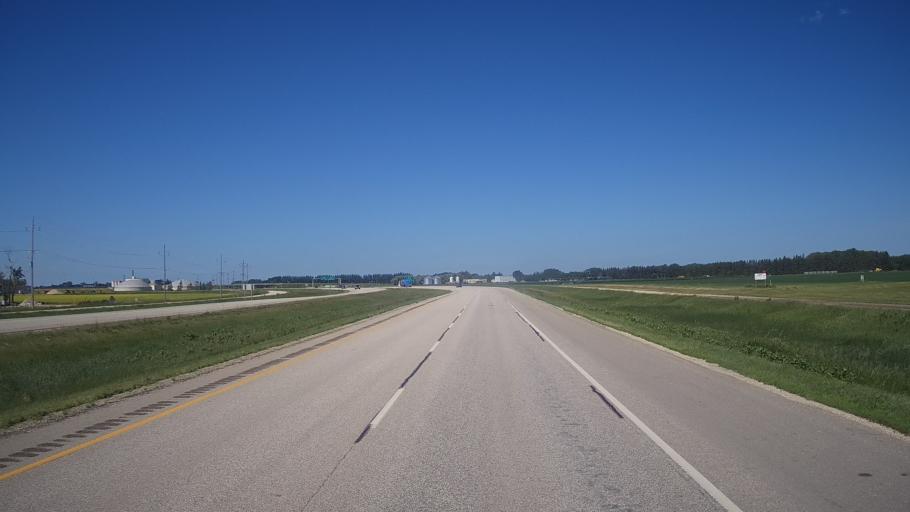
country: CA
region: Manitoba
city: Portage la Prairie
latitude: 49.9590
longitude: -98.2588
